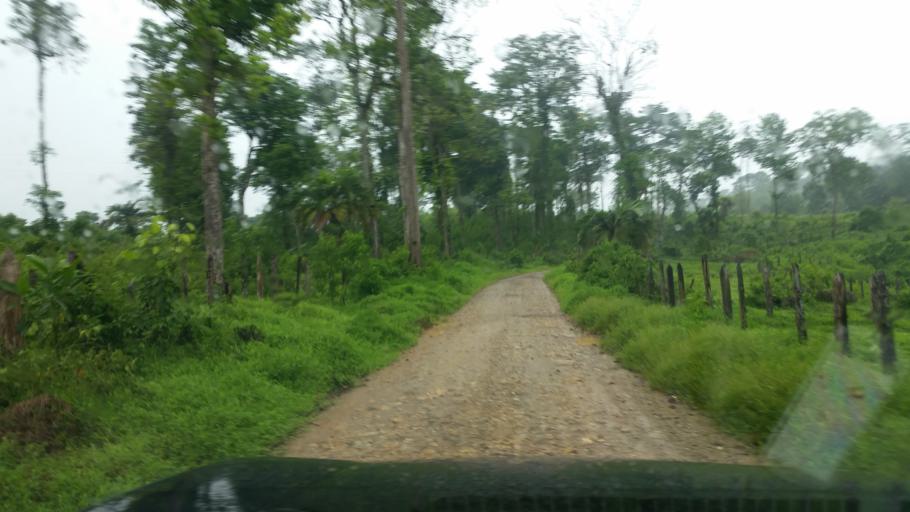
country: NI
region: Atlantico Norte (RAAN)
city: Bonanza
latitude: 14.0811
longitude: -84.6717
